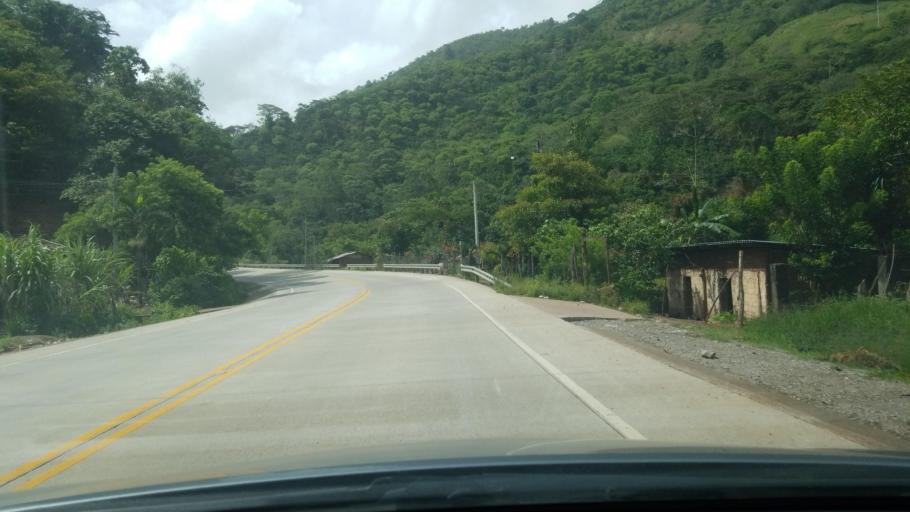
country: HN
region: Copan
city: Buenos Aires
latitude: 14.9318
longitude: -88.9623
